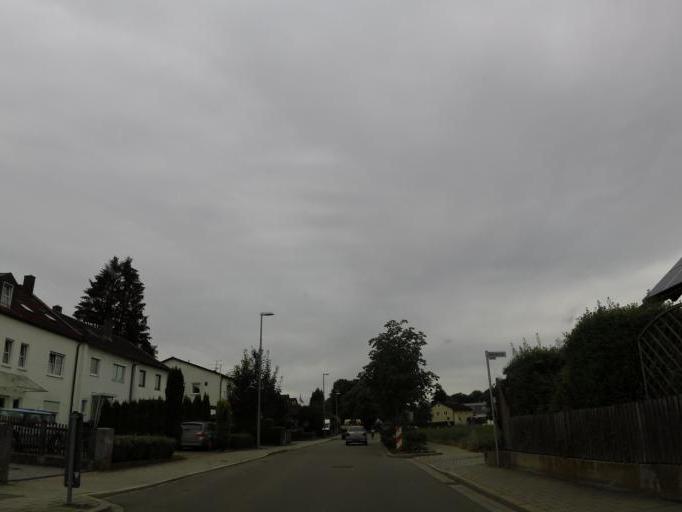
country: DE
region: Bavaria
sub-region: Upper Bavaria
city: Erding
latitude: 48.2927
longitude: 11.9041
